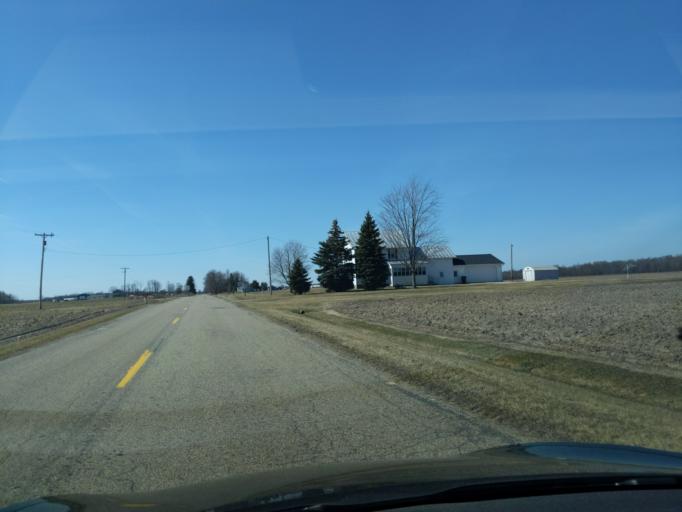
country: US
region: Michigan
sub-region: Ionia County
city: Portland
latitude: 42.7266
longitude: -84.9339
